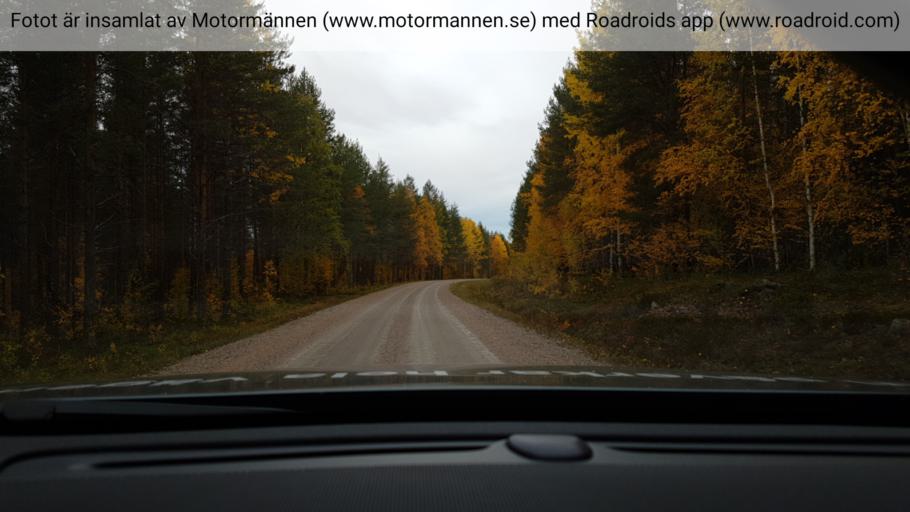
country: SE
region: Norrbotten
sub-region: Overkalix Kommun
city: OEverkalix
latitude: 66.2781
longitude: 22.9809
